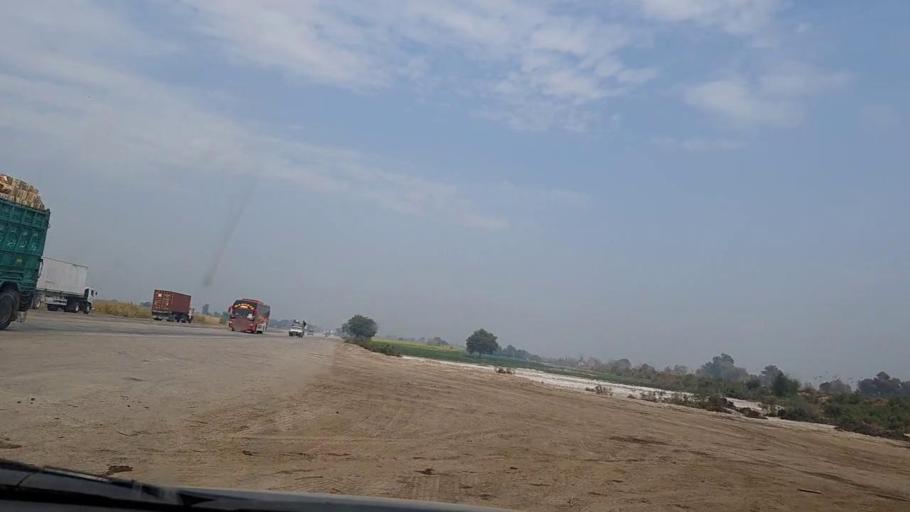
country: PK
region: Sindh
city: Daulatpur
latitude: 26.5284
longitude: 67.9734
